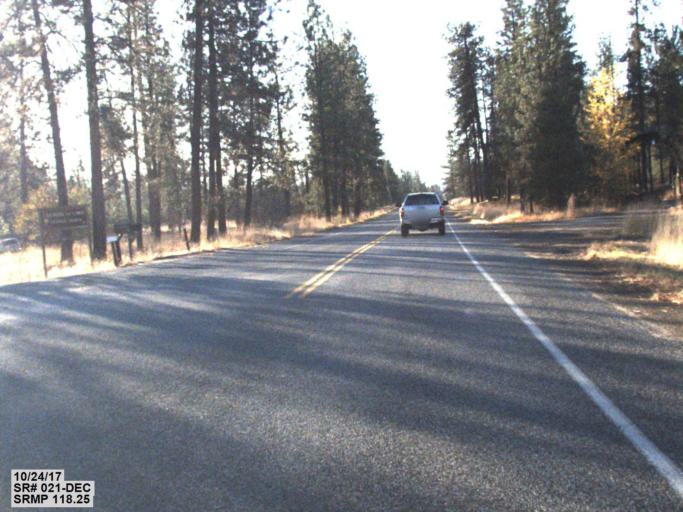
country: US
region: Washington
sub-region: Okanogan County
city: Coulee Dam
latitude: 48.0981
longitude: -118.6944
